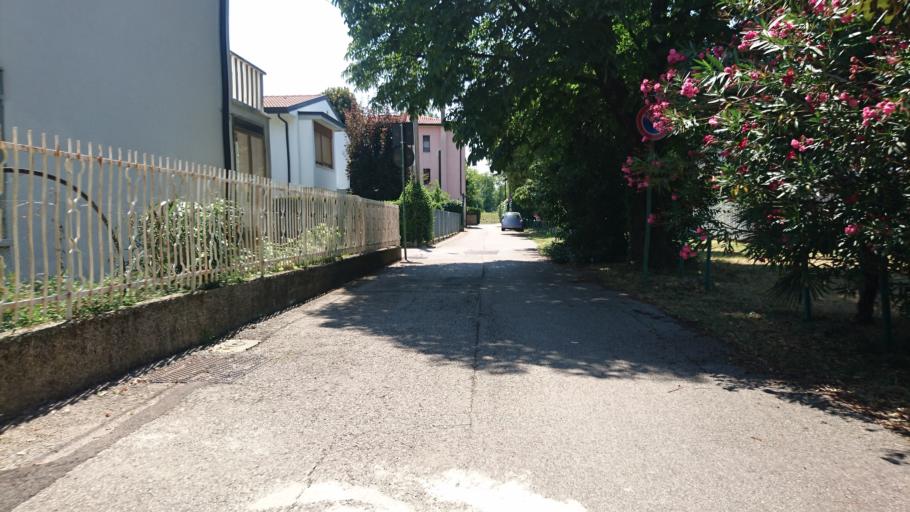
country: IT
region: Veneto
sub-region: Provincia di Padova
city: Padova
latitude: 45.4076
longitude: 11.9080
